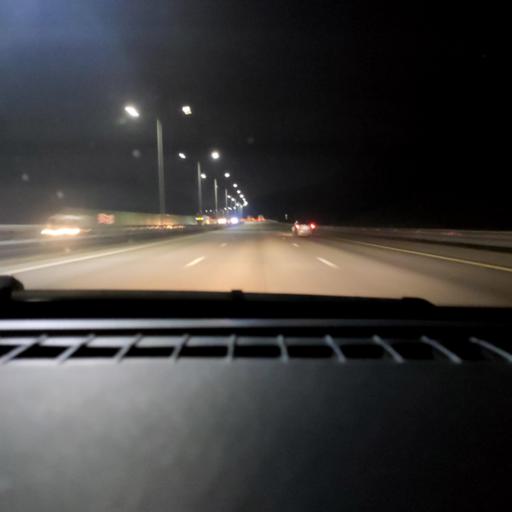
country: RU
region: Voronezj
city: Podgornoye
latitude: 51.8044
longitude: 39.2539
